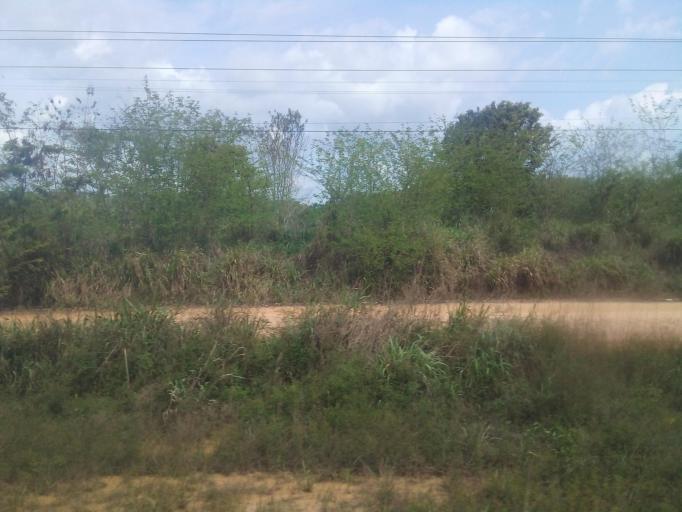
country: BR
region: Maranhao
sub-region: Santa Ines
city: Santa Ines
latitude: -3.8731
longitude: -46.1963
